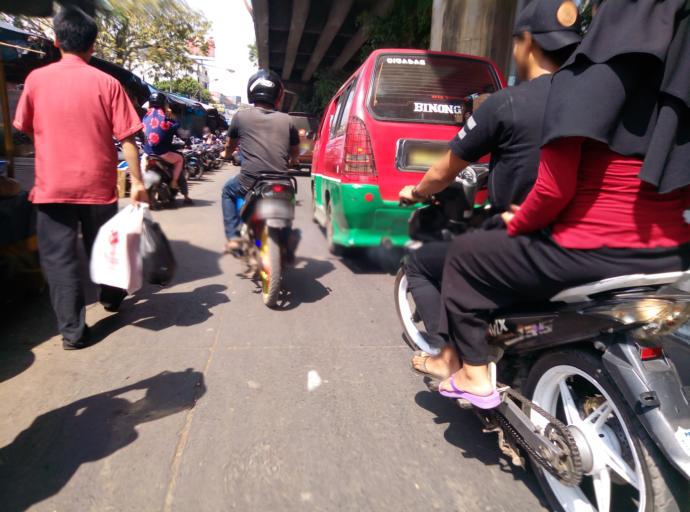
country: ID
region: West Java
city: Bandung
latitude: -6.9257
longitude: 107.6446
